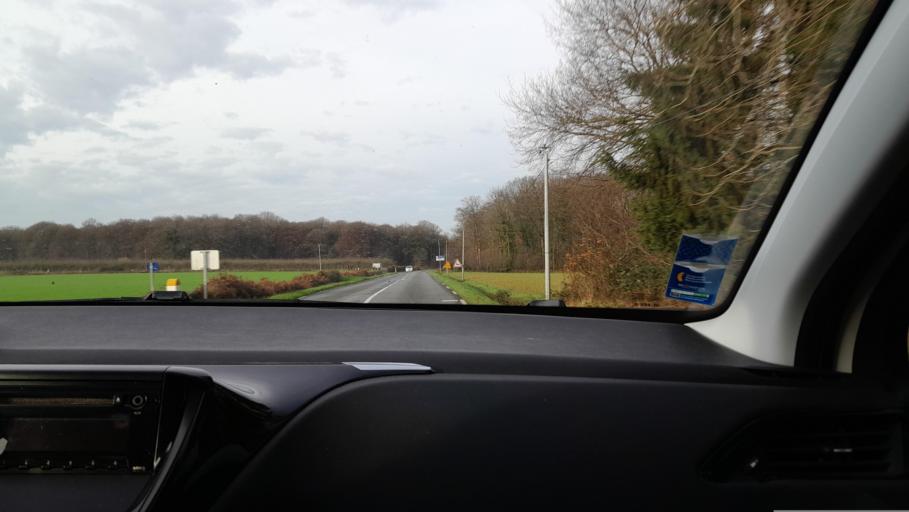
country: FR
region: Brittany
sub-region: Departement d'Ille-et-Vilaine
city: La Guerche-de-Bretagne
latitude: 47.9017
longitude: -1.1761
